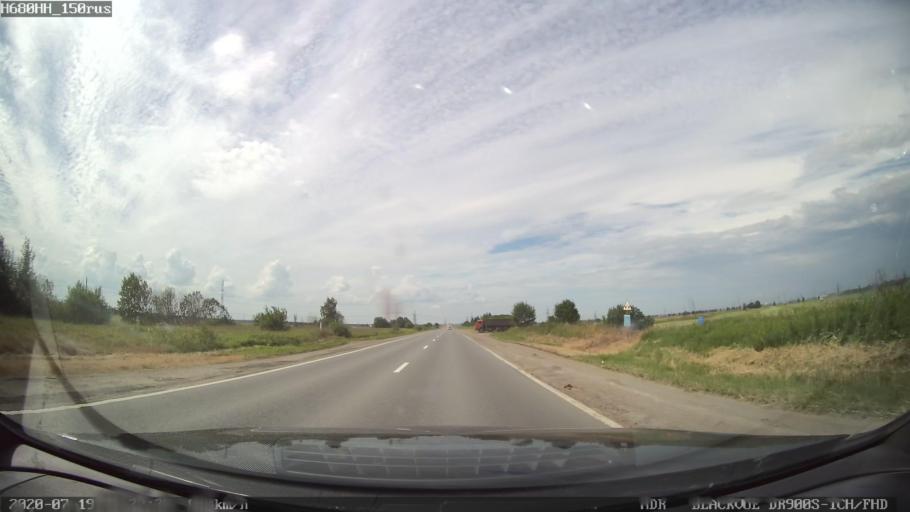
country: RU
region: Leningrad
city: Fedorovskoye
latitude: 59.7047
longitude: 30.5566
